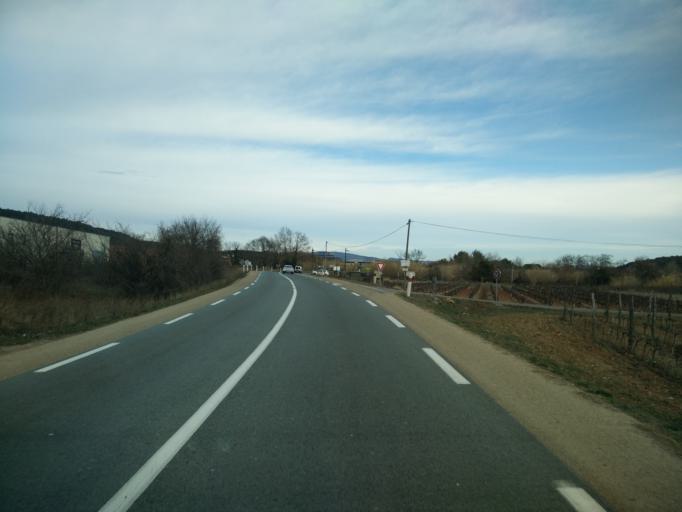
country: FR
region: Provence-Alpes-Cote d'Azur
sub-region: Departement du Var
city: Les Arcs
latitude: 43.4483
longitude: 6.4860
